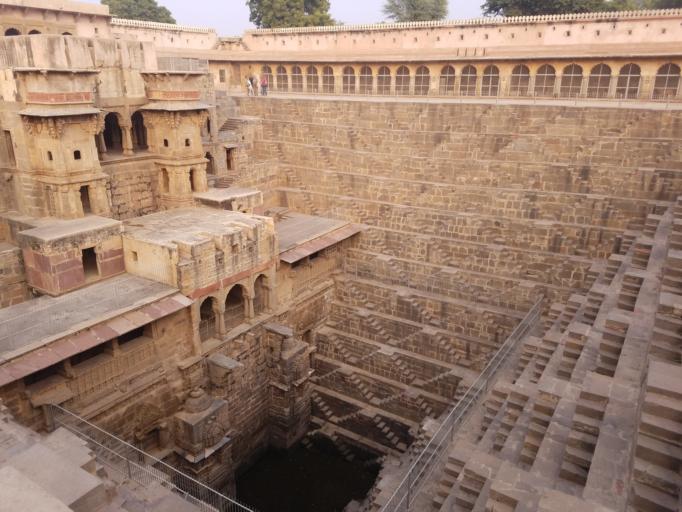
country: IN
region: Rajasthan
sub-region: Dausa
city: Abhaneri
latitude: 27.0071
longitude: 76.6063
